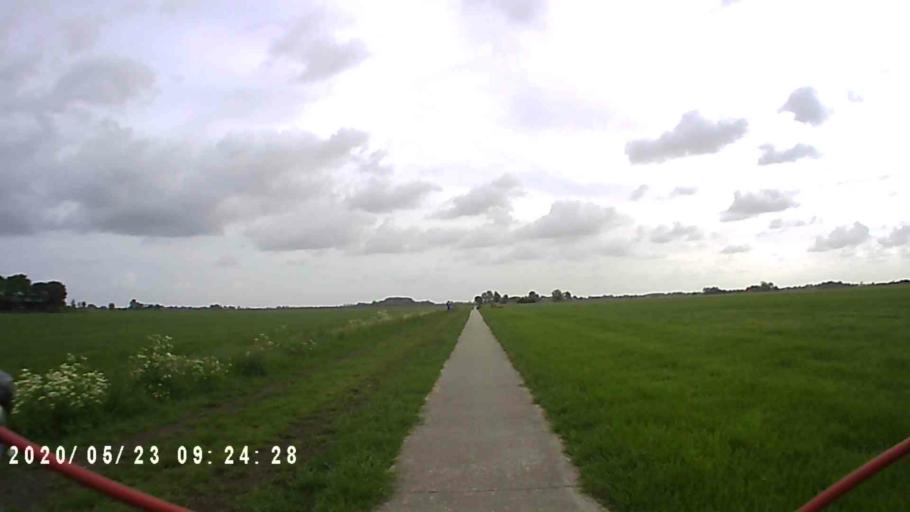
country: NL
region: Groningen
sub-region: Gemeente Bedum
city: Bedum
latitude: 53.2907
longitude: 6.6878
